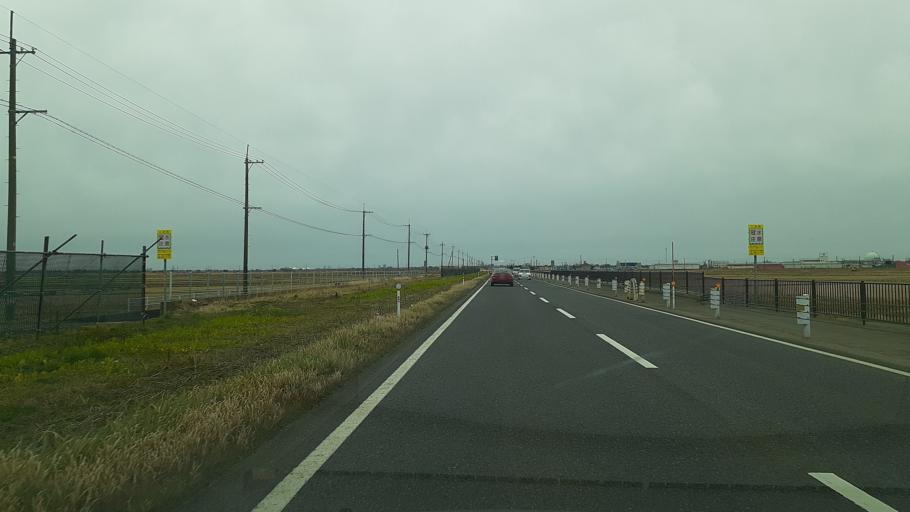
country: JP
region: Niigata
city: Niitsu-honcho
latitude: 37.8065
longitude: 139.1017
